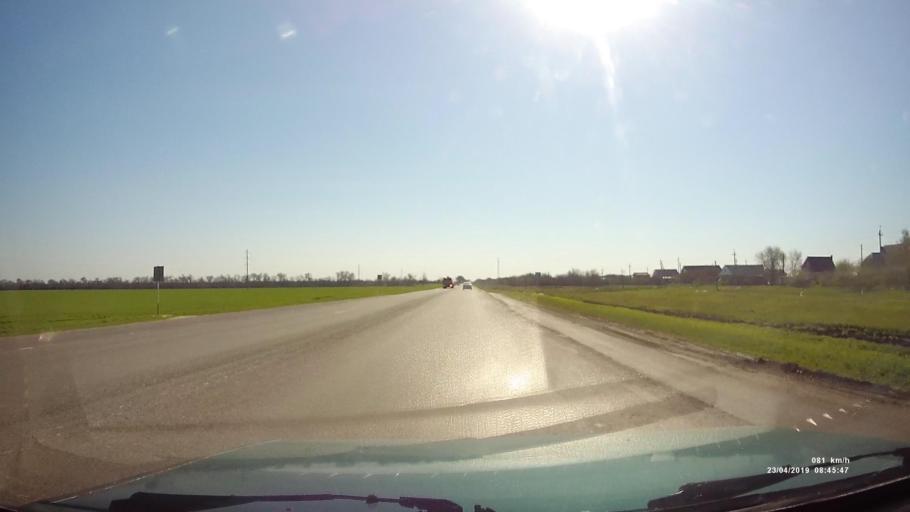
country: RU
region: Rostov
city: Gigant
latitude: 46.5183
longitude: 41.3389
